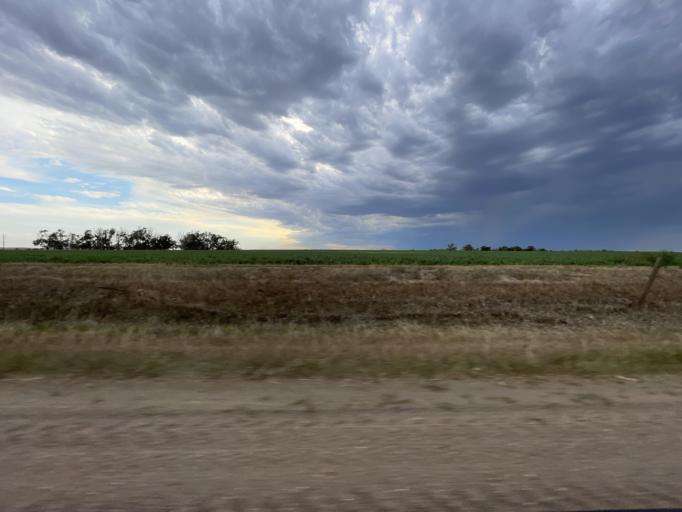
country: US
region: Nebraska
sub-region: Red Willow County
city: McCook
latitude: 40.2522
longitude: -100.7601
